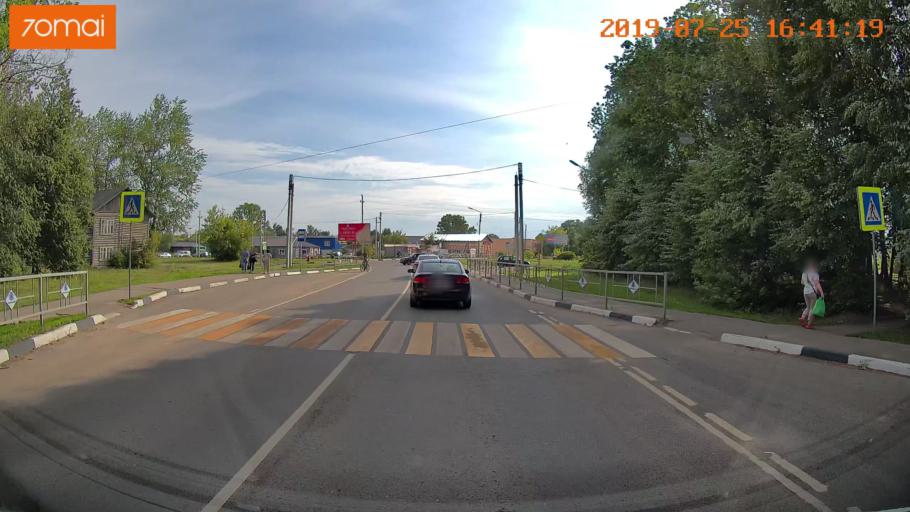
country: RU
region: Ivanovo
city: Privolzhsk
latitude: 57.3811
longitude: 41.2968
